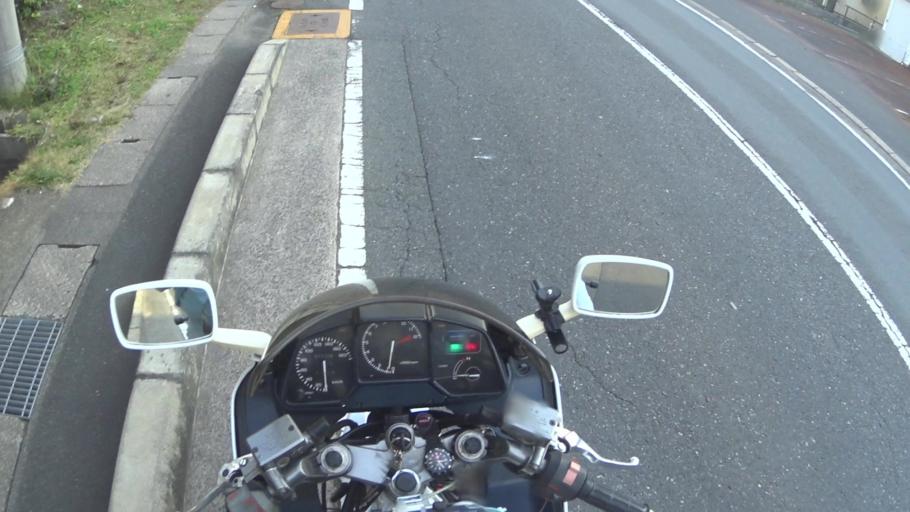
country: JP
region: Kyoto
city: Maizuru
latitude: 35.4834
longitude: 135.4336
